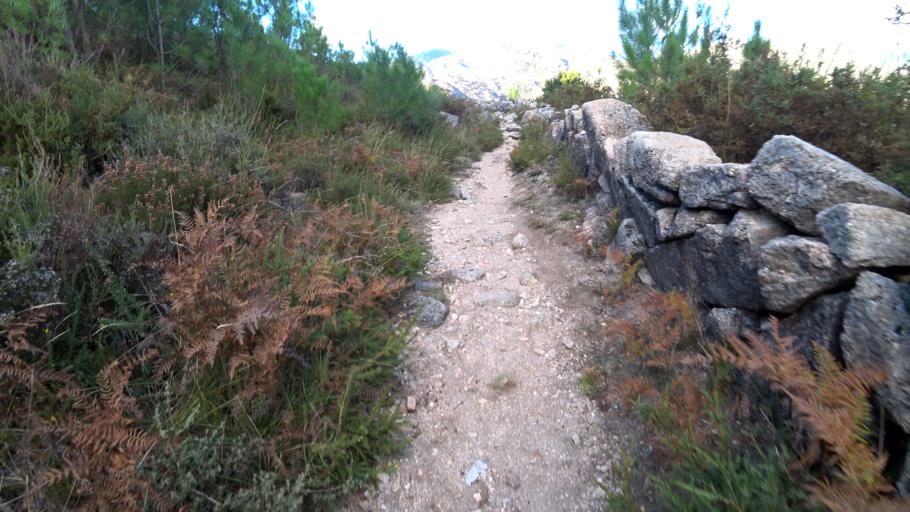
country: PT
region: Braga
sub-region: Terras de Bouro
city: Antas
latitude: 41.7708
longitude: -8.1871
